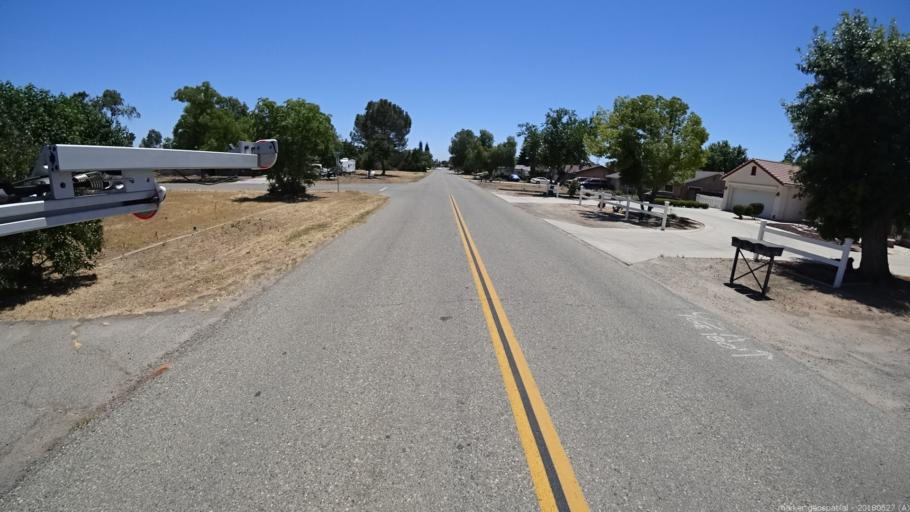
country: US
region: California
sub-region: Madera County
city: Bonadelle Ranchos-Madera Ranchos
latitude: 36.9269
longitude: -119.8761
